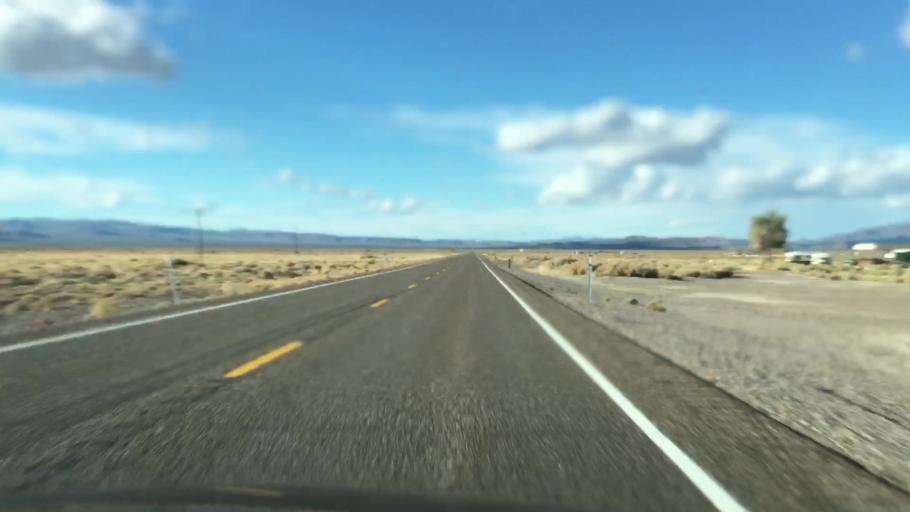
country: US
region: Nevada
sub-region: Nye County
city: Beatty
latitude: 37.2496
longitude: -117.0033
